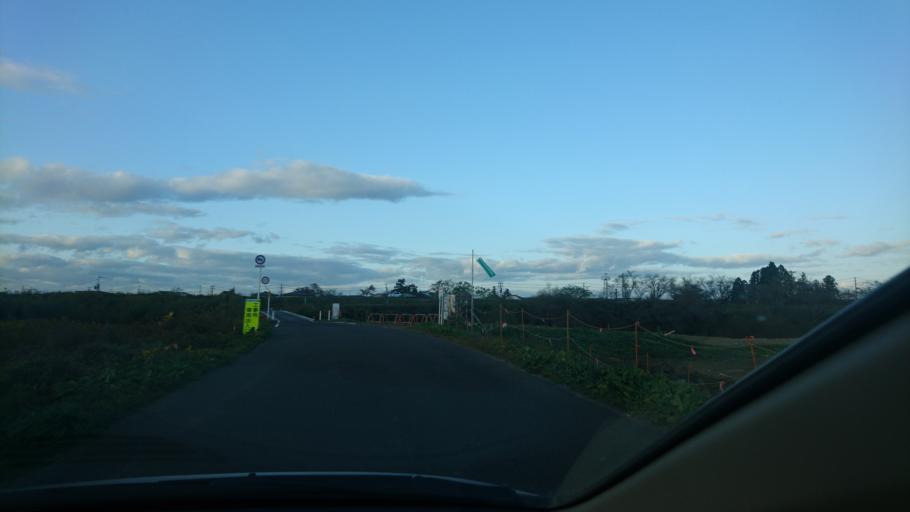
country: JP
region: Iwate
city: Ichinoseki
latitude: 38.7854
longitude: 141.0892
